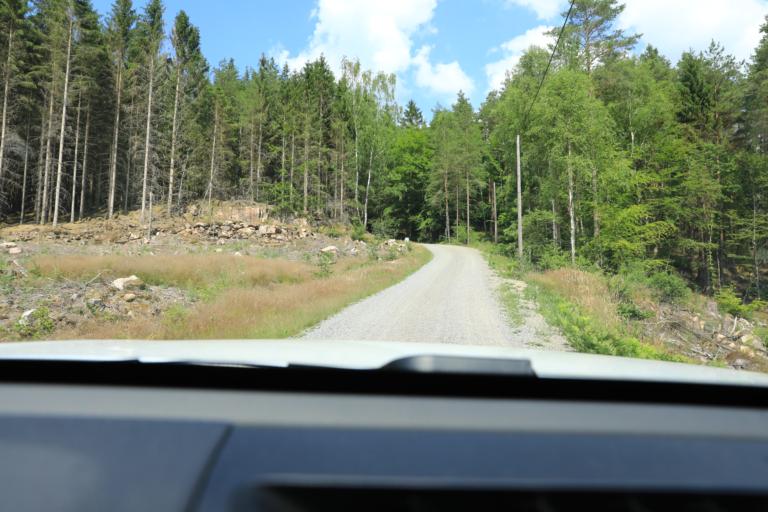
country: SE
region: Halland
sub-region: Varbergs Kommun
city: Veddige
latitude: 57.2127
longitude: 12.3496
